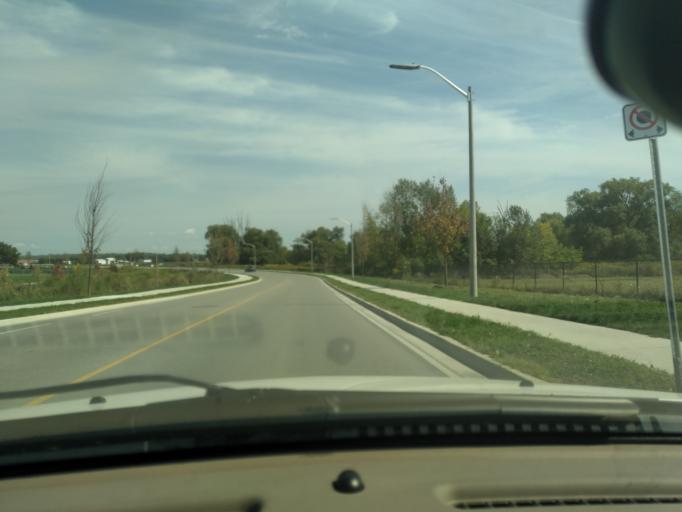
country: CA
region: Ontario
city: Bradford West Gwillimbury
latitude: 44.1101
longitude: -79.5625
